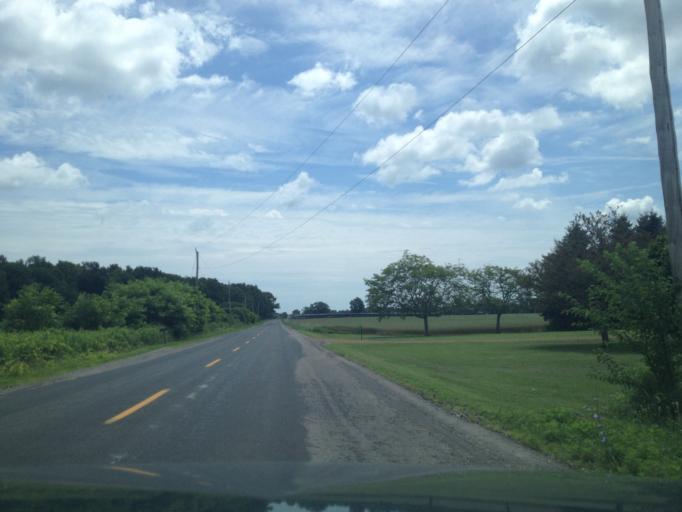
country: CA
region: Ontario
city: Norfolk County
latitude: 42.7909
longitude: -80.3059
